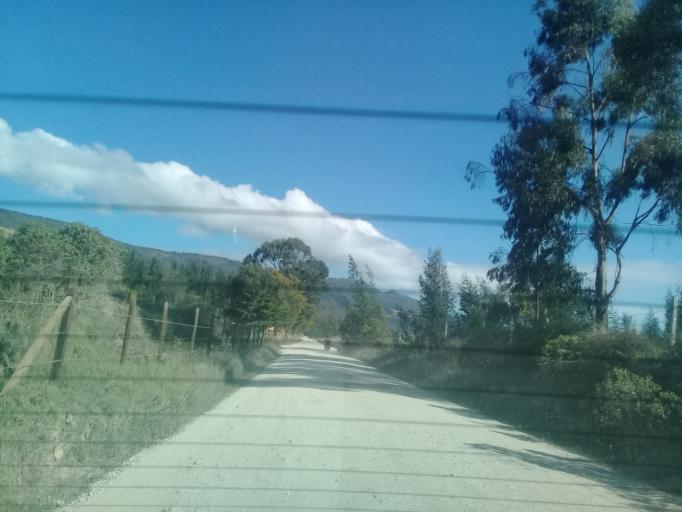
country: CO
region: Cundinamarca
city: Guasca
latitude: 4.9114
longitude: -73.8858
